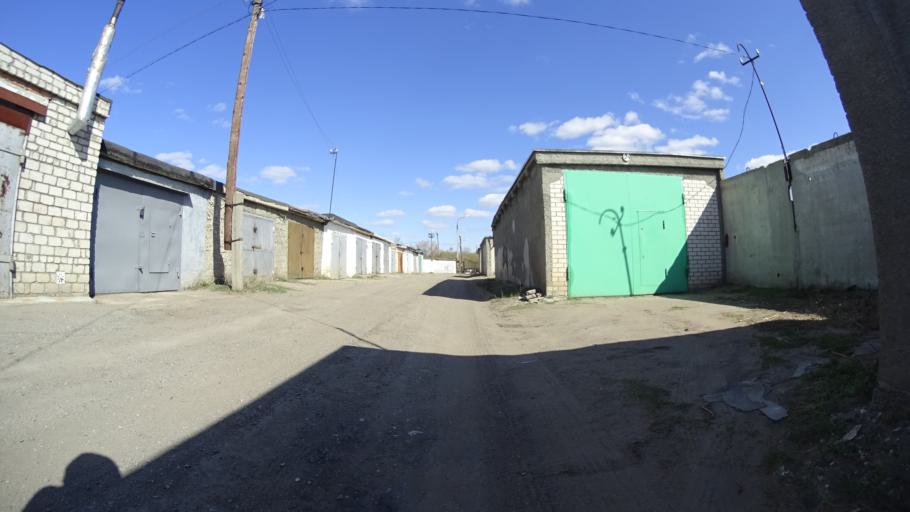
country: RU
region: Chelyabinsk
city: Troitsk
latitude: 54.0827
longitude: 61.5290
